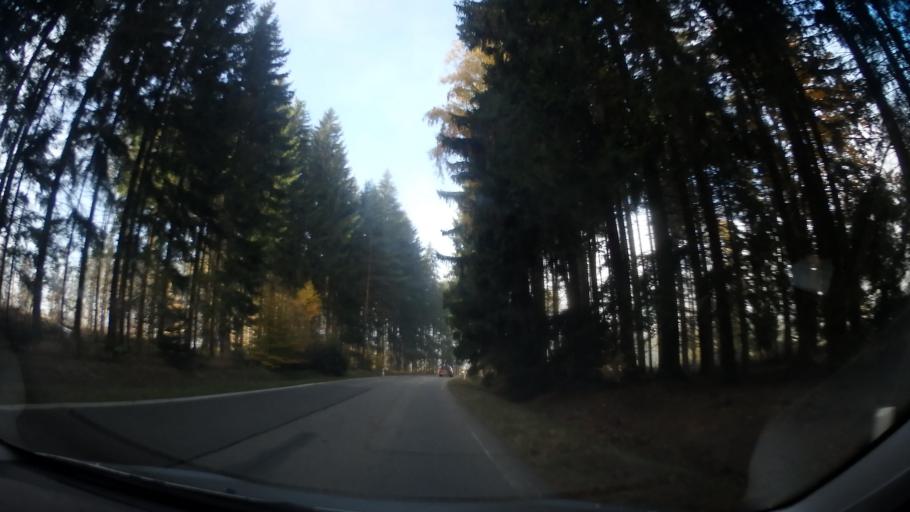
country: CZ
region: Vysocina
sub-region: Okres Zd'ar nad Sazavou
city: Nove Mesto na Morave
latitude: 49.4821
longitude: 16.0149
